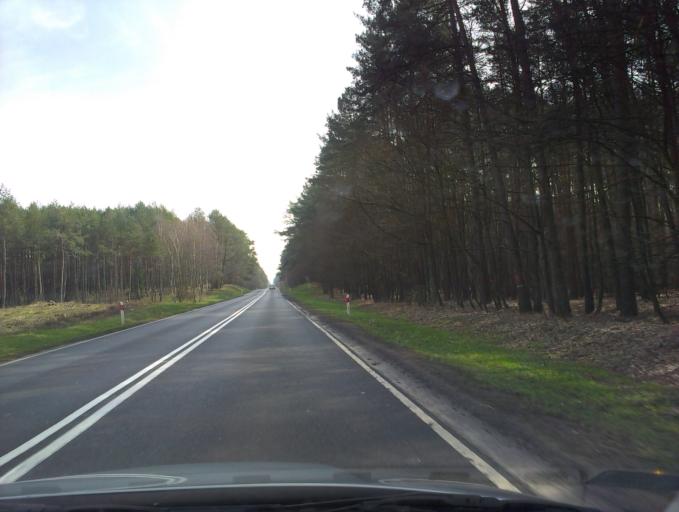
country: PL
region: Greater Poland Voivodeship
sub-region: Powiat pilski
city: Pila
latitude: 53.1470
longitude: 16.8146
